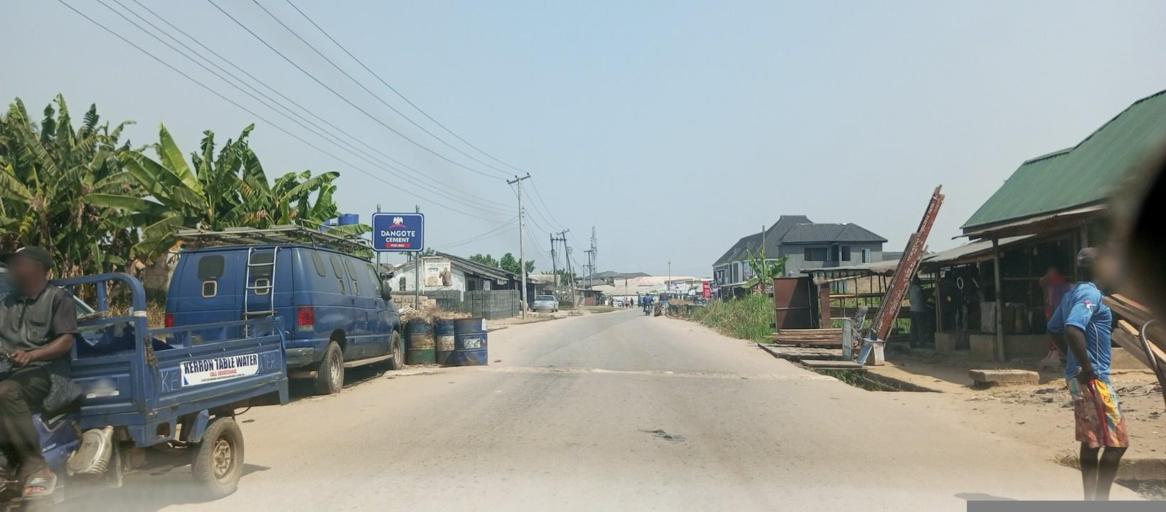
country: NG
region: Rivers
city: Emuoha
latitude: 4.9156
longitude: 6.9155
